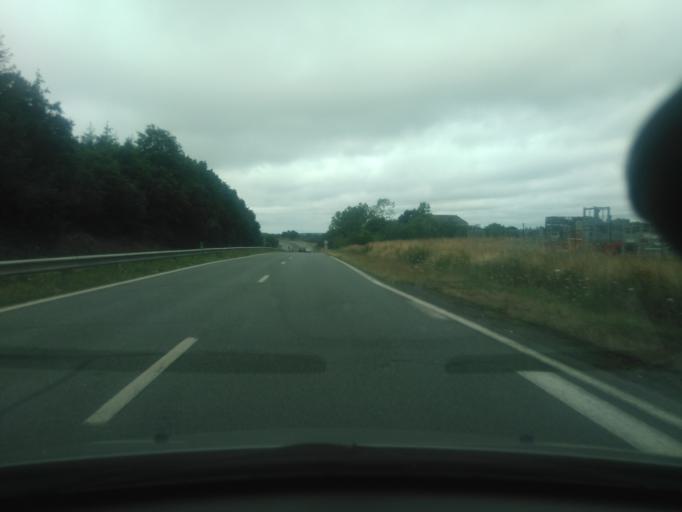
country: FR
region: Brittany
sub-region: Departement des Cotes-d'Armor
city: Jugon-les-Lacs
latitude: 48.4098
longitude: -2.3513
